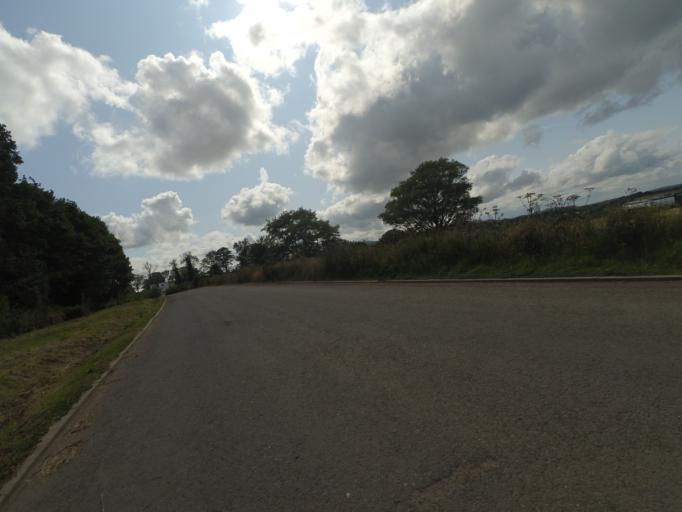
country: GB
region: Scotland
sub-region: Midlothian
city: Bonnyrigg
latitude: 55.9181
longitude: -3.1222
